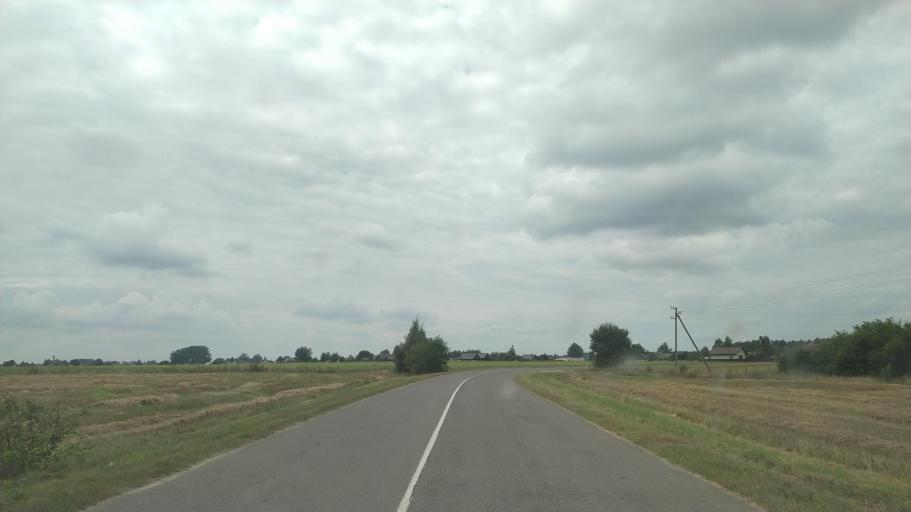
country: BY
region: Brest
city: Byelaazyorsk
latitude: 52.5411
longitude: 25.1138
